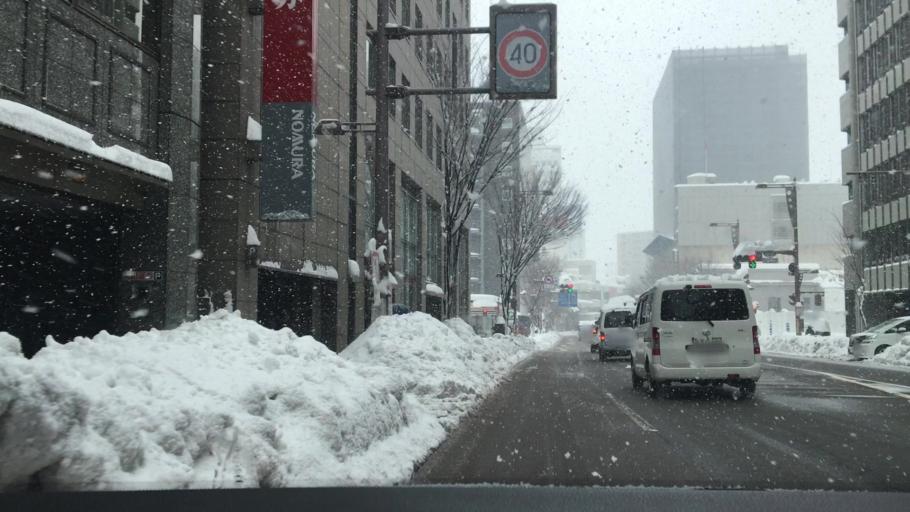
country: JP
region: Ishikawa
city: Kanazawa-shi
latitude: 36.5692
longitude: 136.6544
